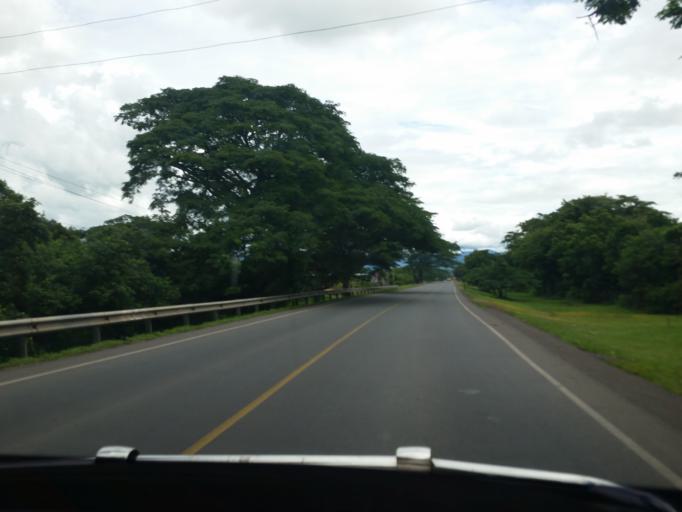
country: NI
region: Matagalpa
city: Ciudad Dario
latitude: 12.8228
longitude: -86.1205
